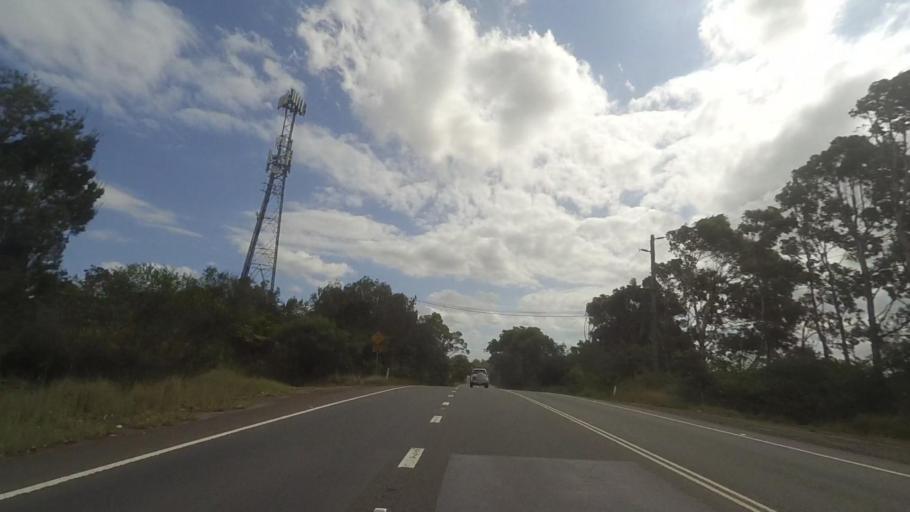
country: AU
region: New South Wales
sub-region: Sutherland Shire
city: Menai
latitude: -34.0392
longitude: 150.9986
